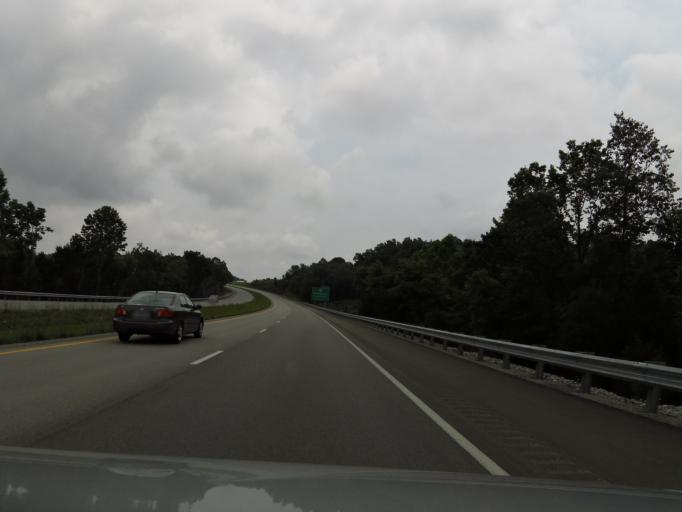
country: US
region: Kentucky
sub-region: Grayson County
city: Leitchfield
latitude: 37.4525
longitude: -86.3225
